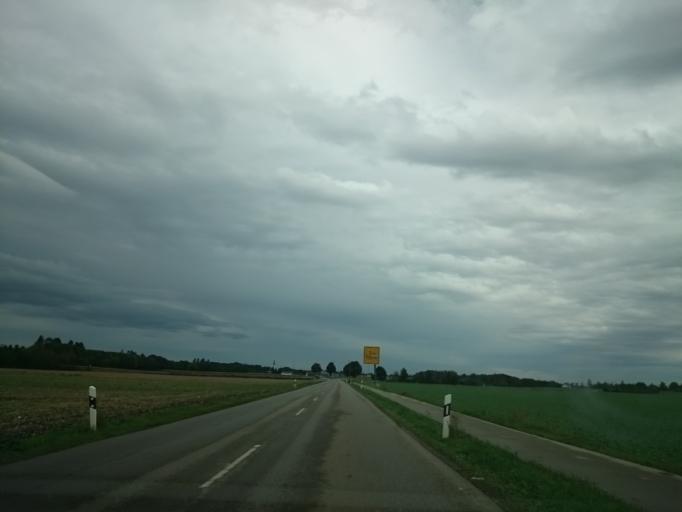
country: DE
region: Bavaria
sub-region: Swabia
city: Untermeitingen
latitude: 48.1721
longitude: 10.8118
